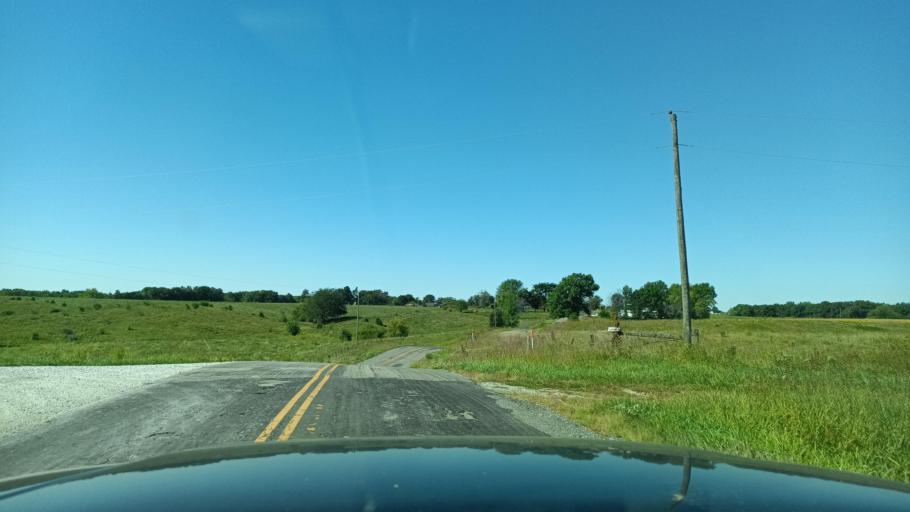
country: US
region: Missouri
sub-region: Scotland County
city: Memphis
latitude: 40.3541
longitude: -92.2932
